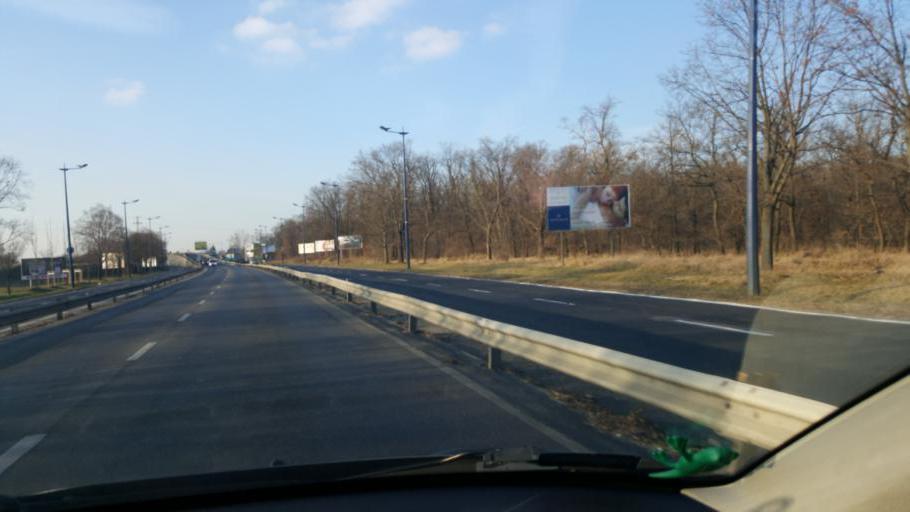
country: HU
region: Budapest
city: Budapest XVIII. keruelet
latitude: 47.4511
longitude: 19.2013
